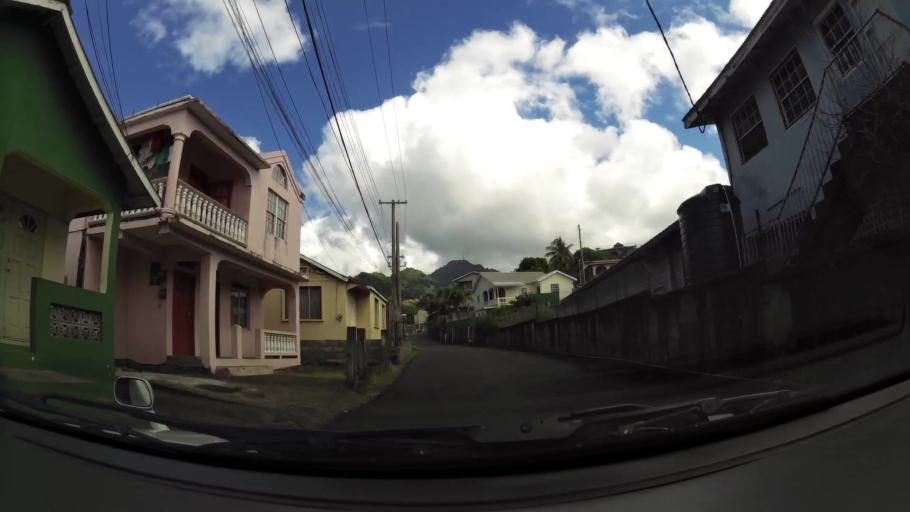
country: VC
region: Saint George
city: Kingstown
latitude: 13.1592
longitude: -61.2281
